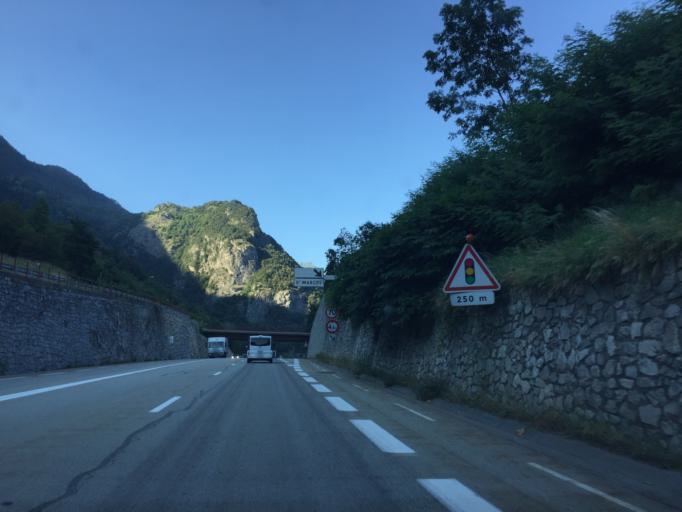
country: FR
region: Rhone-Alpes
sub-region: Departement de la Savoie
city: Moutiers
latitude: 45.5121
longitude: 6.5658
